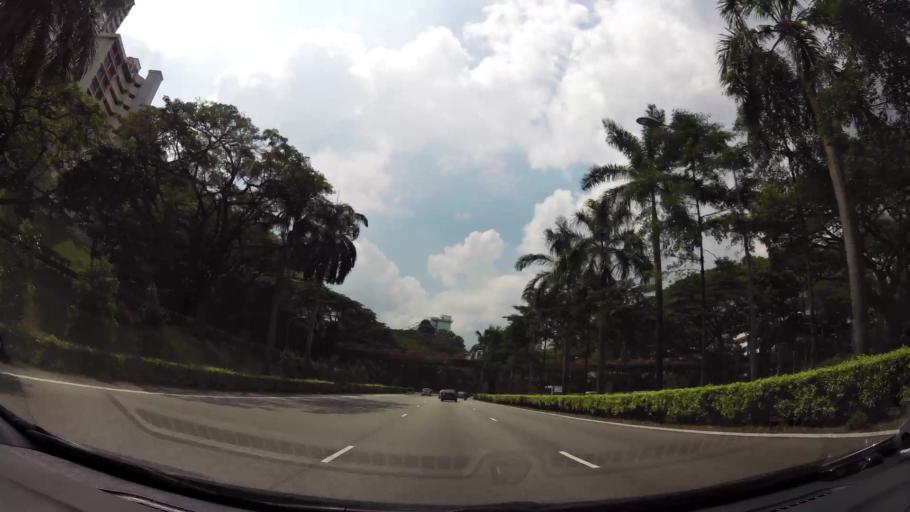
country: SG
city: Singapore
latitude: 1.2788
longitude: 103.8220
